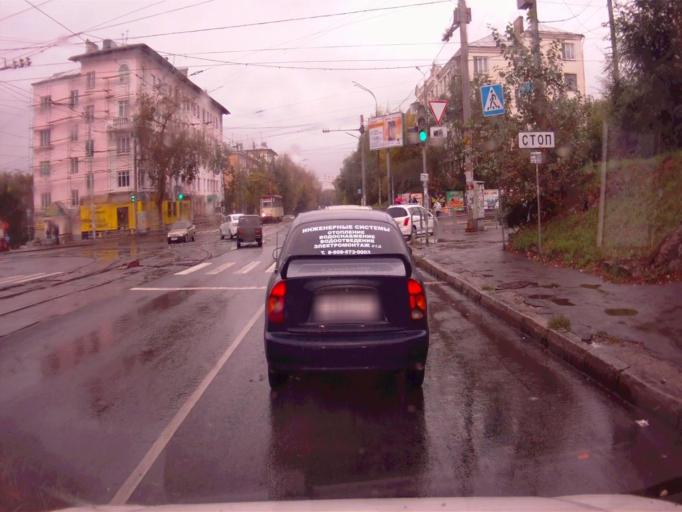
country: RU
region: Chelyabinsk
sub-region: Gorod Chelyabinsk
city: Chelyabinsk
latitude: 55.1850
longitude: 61.4143
